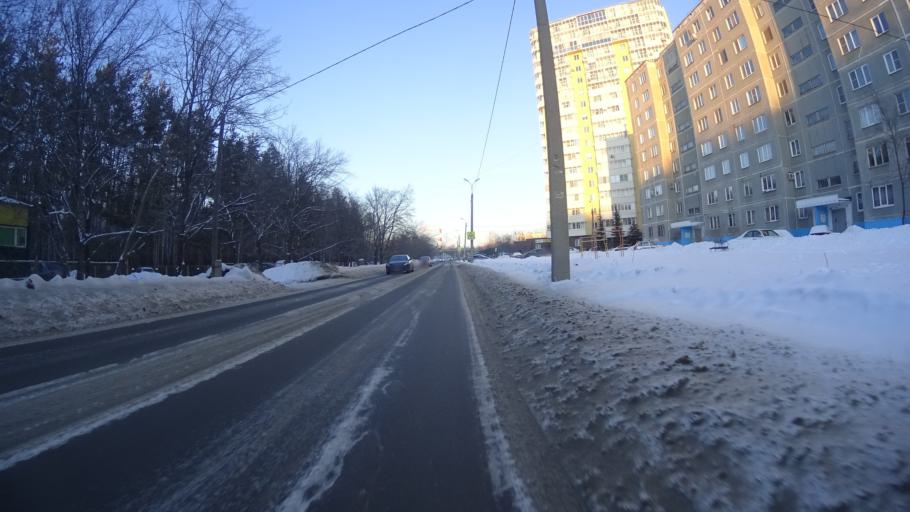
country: RU
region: Chelyabinsk
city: Roshchino
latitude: 55.1970
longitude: 61.2992
